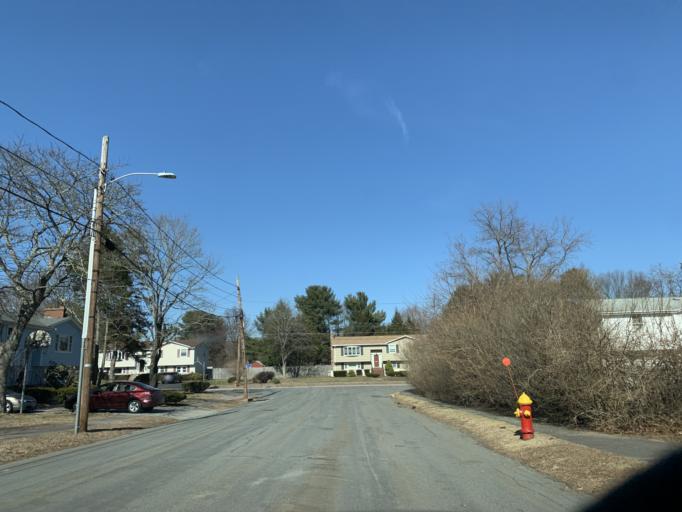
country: US
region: Massachusetts
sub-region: Norfolk County
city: Westwood
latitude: 42.1929
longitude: -71.2255
